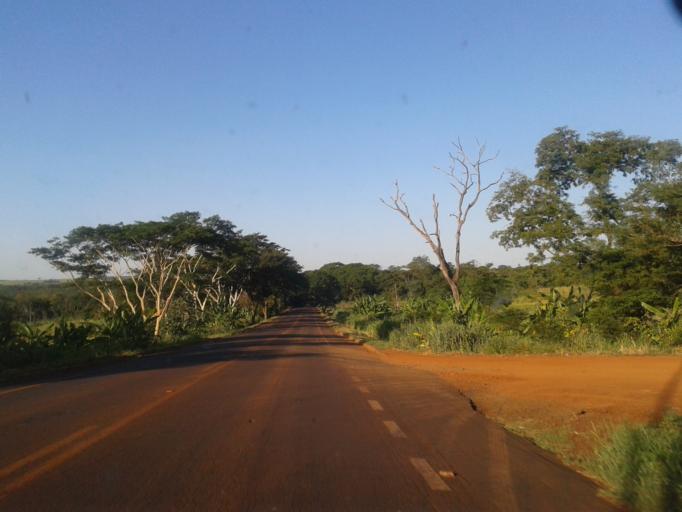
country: BR
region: Minas Gerais
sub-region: Capinopolis
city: Capinopolis
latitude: -18.6915
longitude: -49.6178
